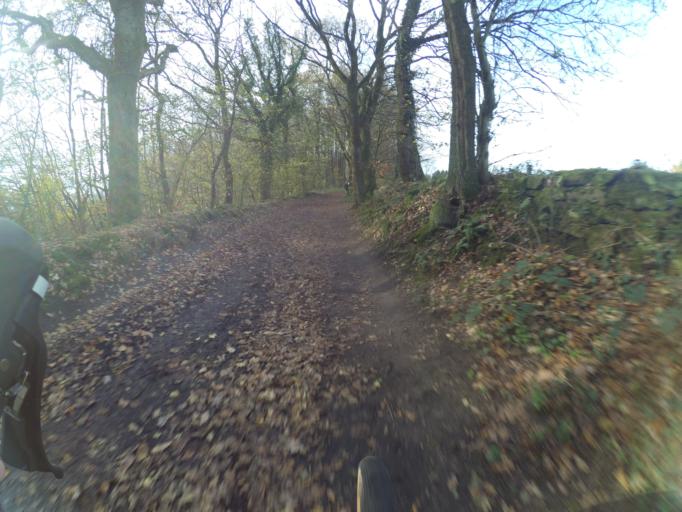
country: DE
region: North Rhine-Westphalia
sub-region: Regierungsbezirk Munster
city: Tecklenburg
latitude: 52.2211
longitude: 7.7972
